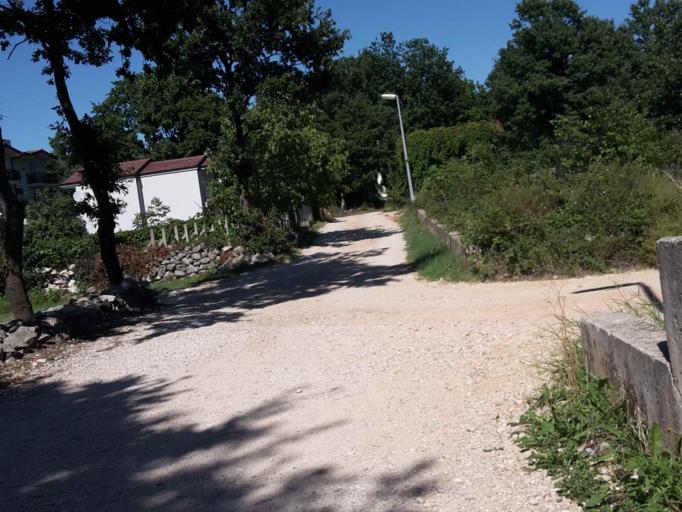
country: BA
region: Federation of Bosnia and Herzegovina
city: Citluk
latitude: 43.1928
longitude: 17.6752
